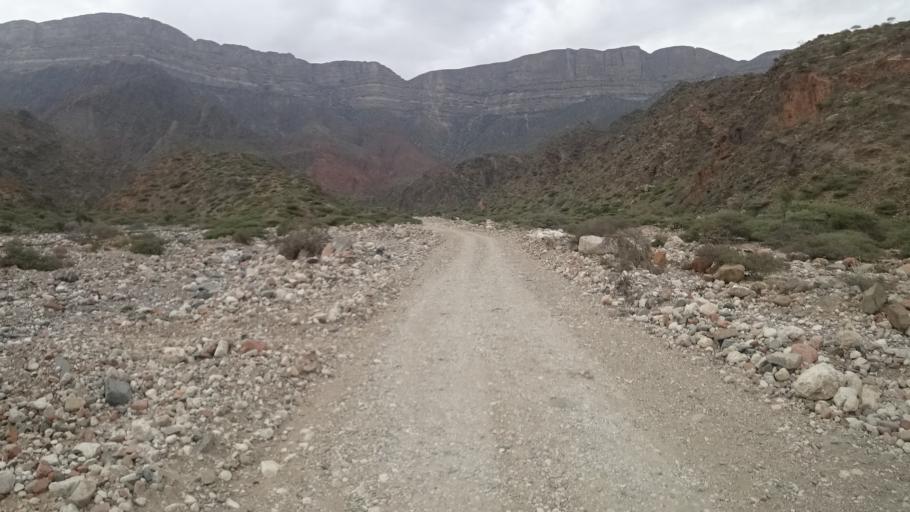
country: OM
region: Zufar
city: Salalah
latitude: 17.1790
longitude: 54.9481
